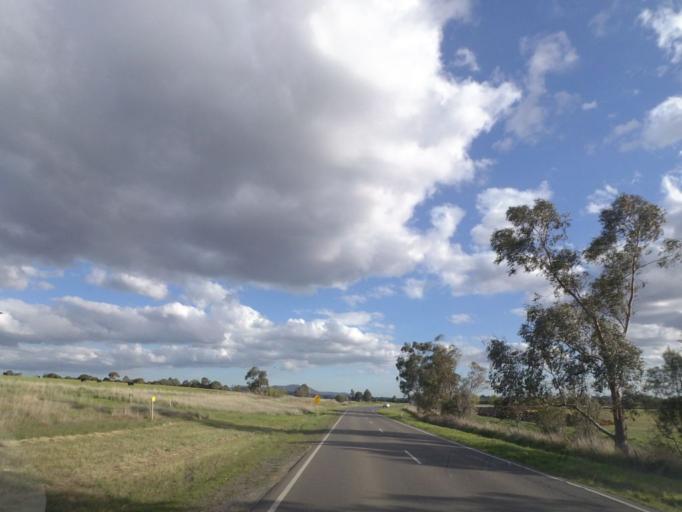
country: AU
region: Victoria
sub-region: Yarra Ranges
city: Yarra Glen
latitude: -37.6971
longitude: 145.3726
